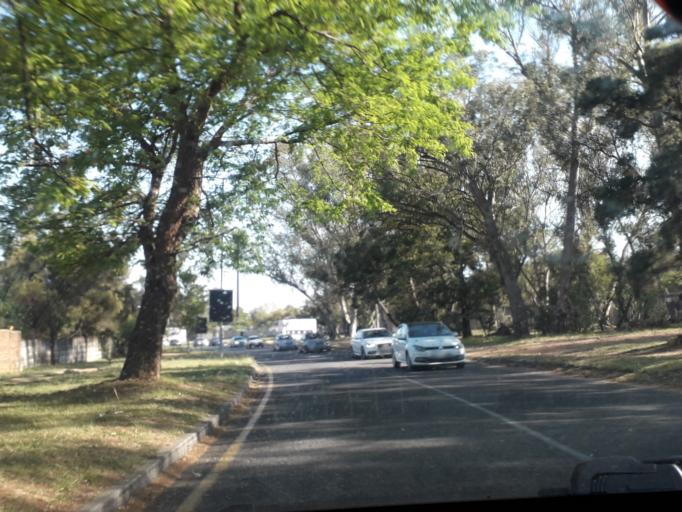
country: ZA
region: Gauteng
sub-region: City of Johannesburg Metropolitan Municipality
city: Midrand
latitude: -26.0500
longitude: 28.0719
